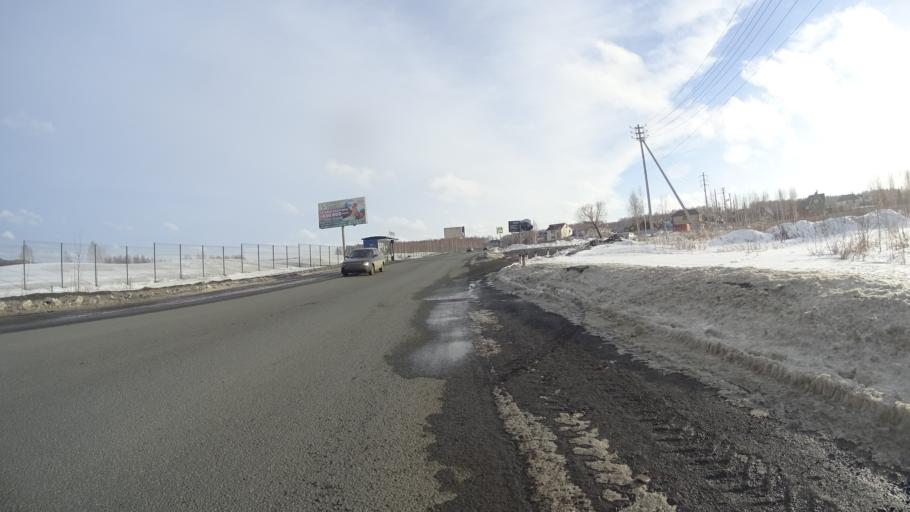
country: RU
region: Chelyabinsk
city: Sargazy
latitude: 55.1345
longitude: 61.2856
